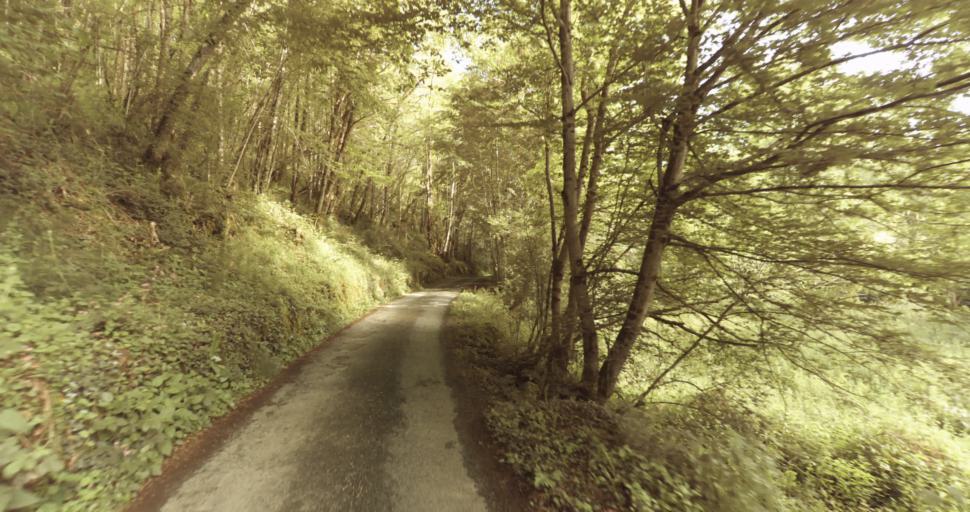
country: FR
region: Limousin
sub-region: Departement de la Haute-Vienne
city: Le Vigen
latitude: 45.7478
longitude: 1.2866
